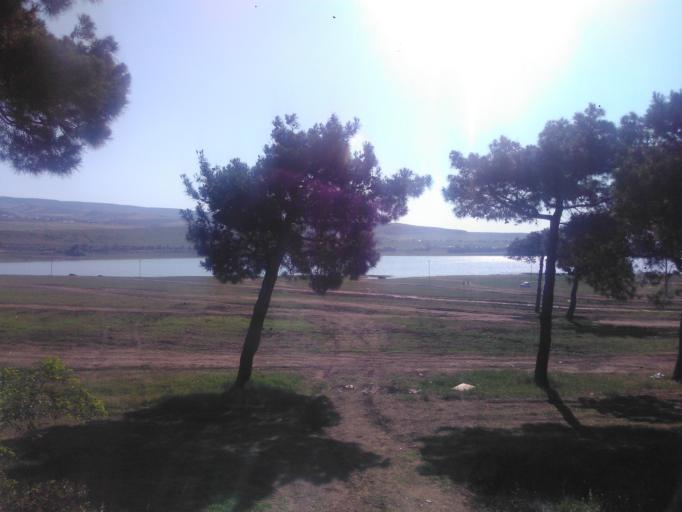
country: GE
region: T'bilisi
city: Tbilisi
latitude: 41.7184
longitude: 44.8766
